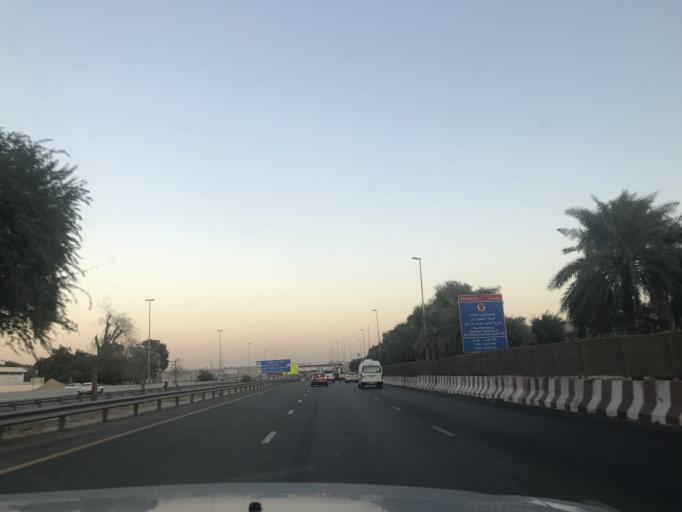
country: AE
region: Ash Shariqah
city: Sharjah
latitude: 25.1811
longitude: 55.3897
